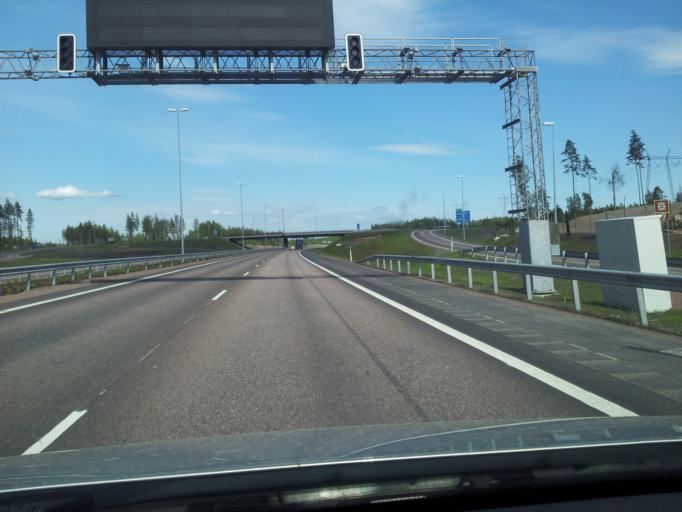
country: FI
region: Uusimaa
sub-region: Loviisa
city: Ruotsinpyhtaeae
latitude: 60.4913
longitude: 26.4143
